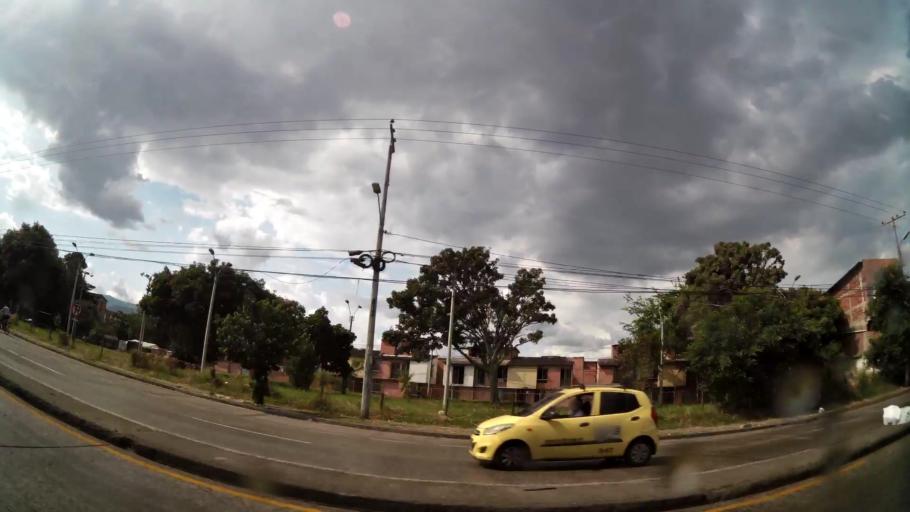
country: CO
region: Valle del Cauca
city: Cali
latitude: 3.4641
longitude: -76.4961
